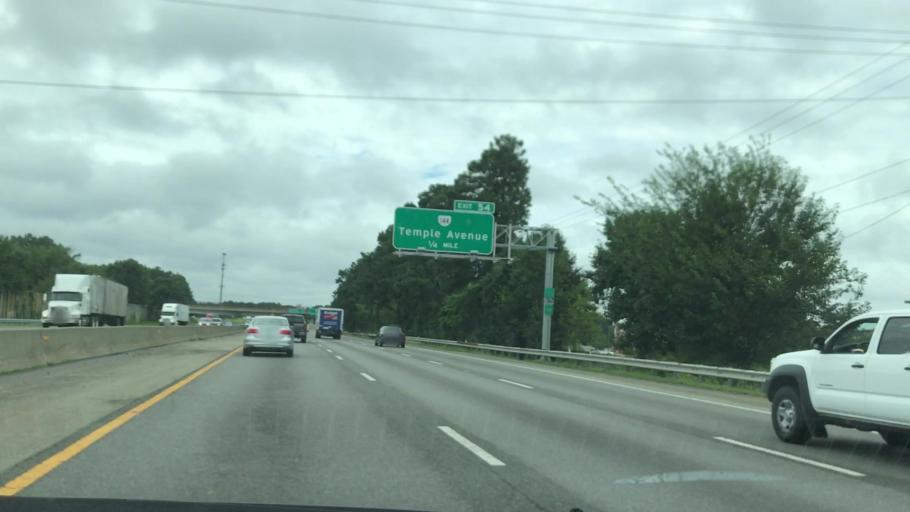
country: US
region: Virginia
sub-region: City of Colonial Heights
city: Colonial Heights
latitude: 37.2512
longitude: -77.3947
